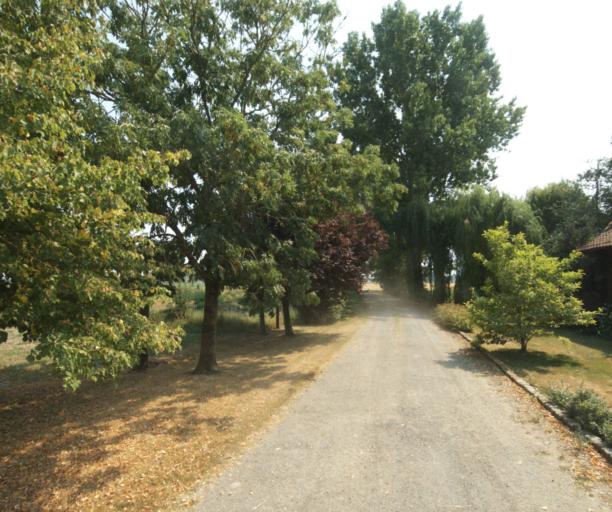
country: FR
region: Nord-Pas-de-Calais
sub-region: Departement du Nord
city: Linselles
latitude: 50.7192
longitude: 3.0497
